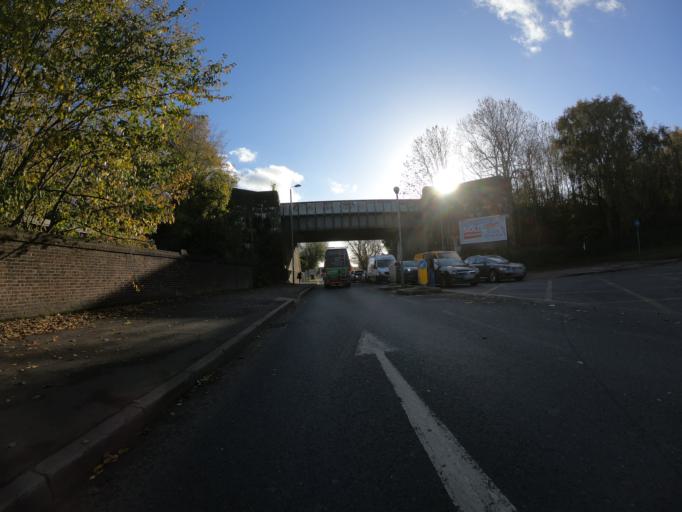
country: GB
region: England
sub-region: Greater London
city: Orpington
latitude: 51.3951
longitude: 0.1120
